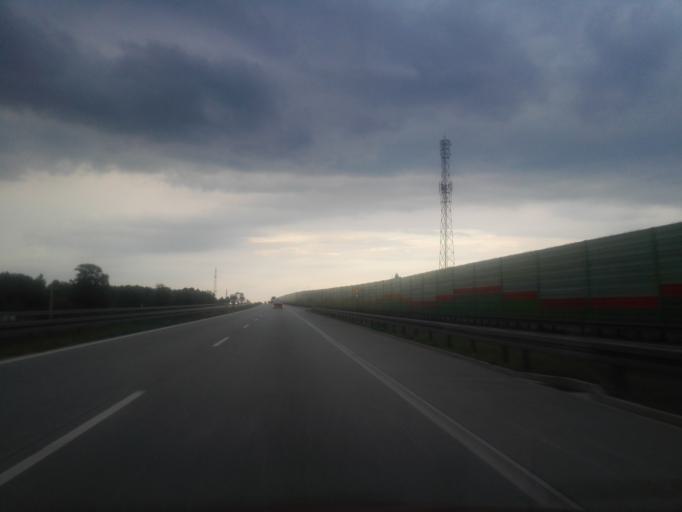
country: PL
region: Lodz Voivodeship
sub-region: Piotrkow Trybunalski
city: Piotrkow Trybunalski
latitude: 51.4421
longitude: 19.6829
